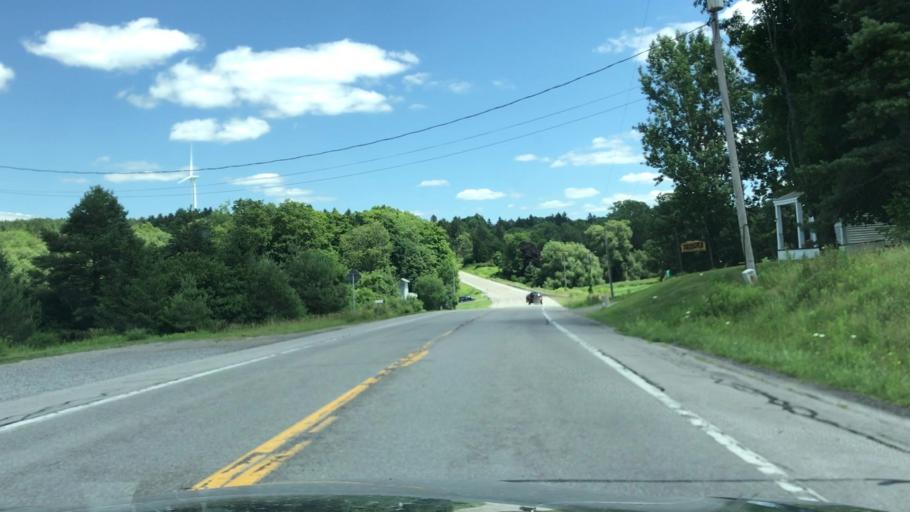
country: US
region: New York
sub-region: Wyoming County
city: Warsaw
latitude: 42.7497
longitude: -78.2460
